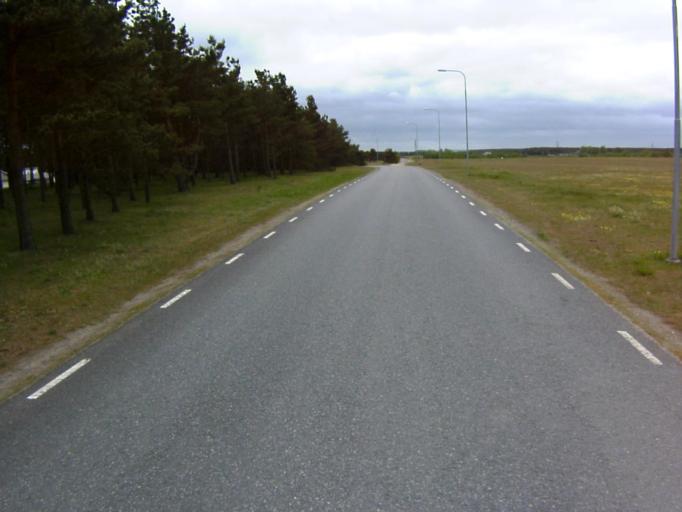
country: SE
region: Skane
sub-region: Kristianstads Kommun
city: Ahus
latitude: 55.9381
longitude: 14.2674
